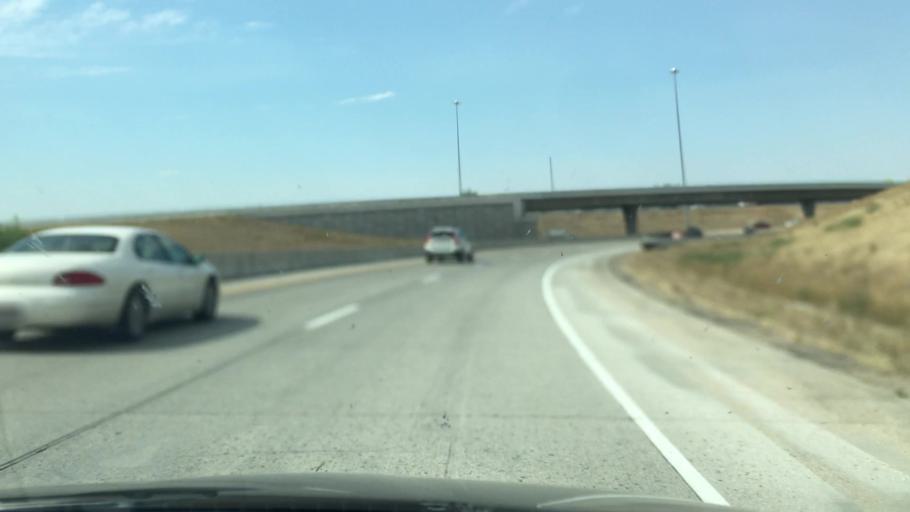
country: US
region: Idaho
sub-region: Ada County
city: Garden City
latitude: 43.5970
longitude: -116.2859
